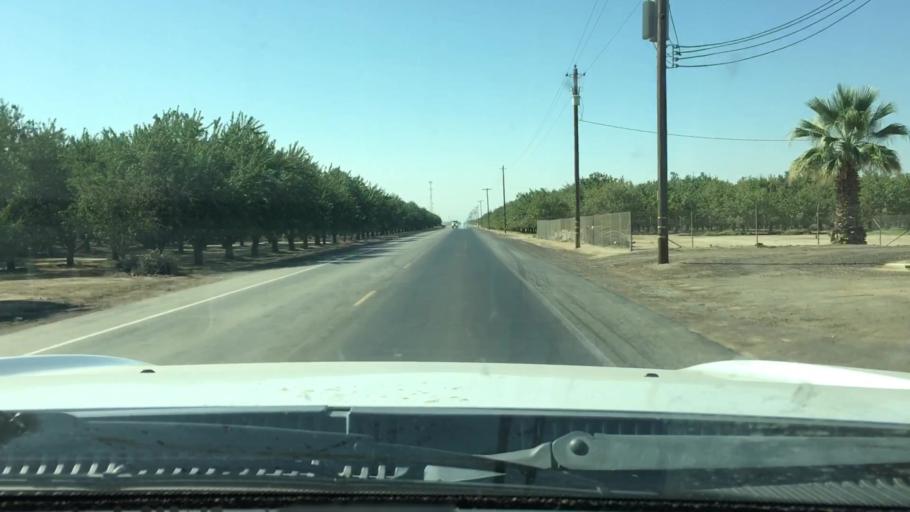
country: US
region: California
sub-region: Kern County
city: Wasco
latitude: 35.5976
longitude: -119.4736
